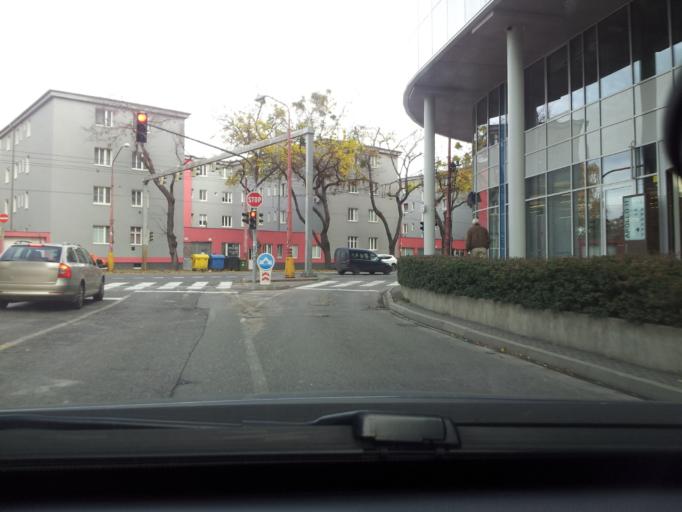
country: SK
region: Bratislavsky
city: Bratislava
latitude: 48.1460
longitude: 17.1380
